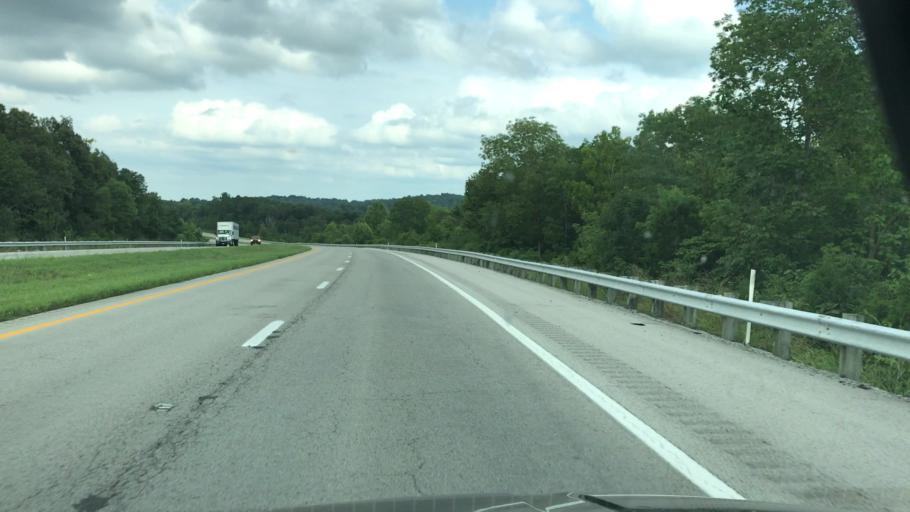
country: US
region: Kentucky
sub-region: Caldwell County
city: Princeton
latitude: 37.1411
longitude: -87.8107
